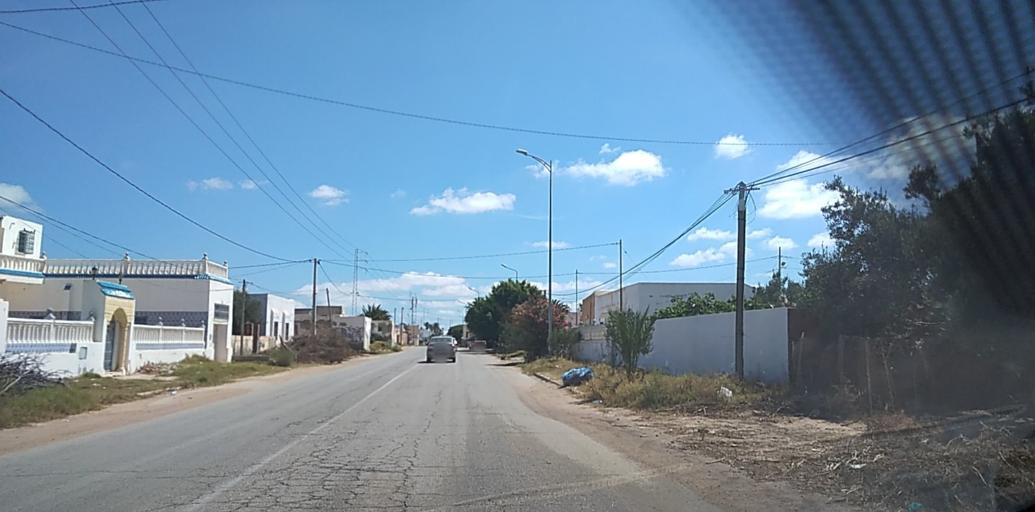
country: TN
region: Safaqis
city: Al Qarmadah
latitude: 34.6706
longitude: 11.1364
